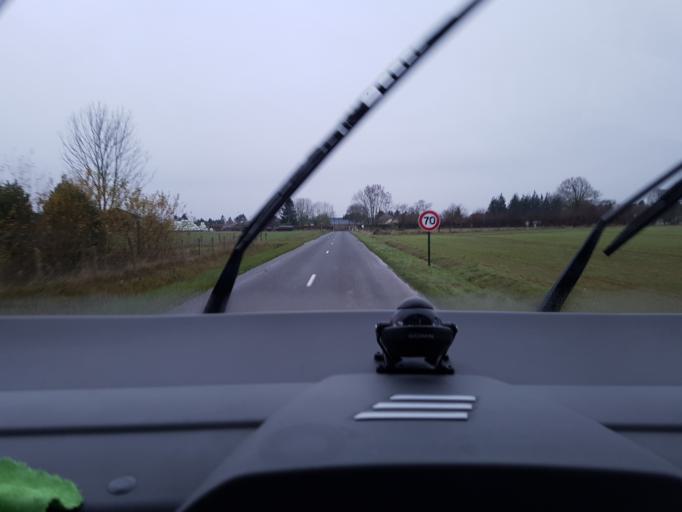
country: FR
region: Haute-Normandie
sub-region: Departement de l'Eure
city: Le Neubourg
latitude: 49.1888
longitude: 0.9564
